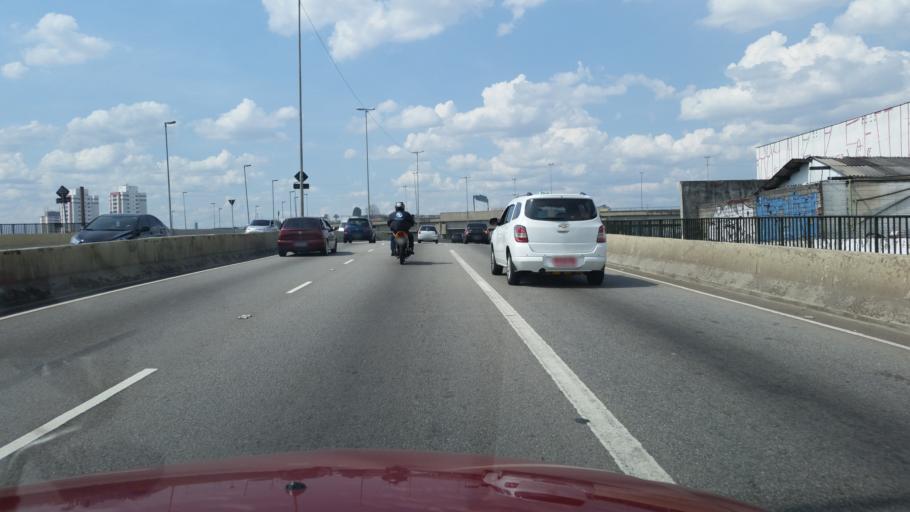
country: BR
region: Sao Paulo
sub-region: Ferraz De Vasconcelos
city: Ferraz de Vasconcelos
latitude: -23.5362
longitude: -46.4548
